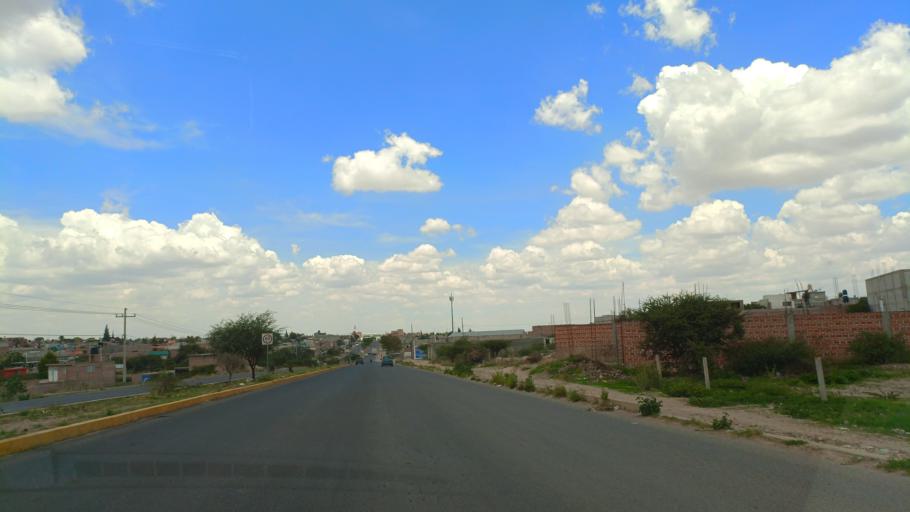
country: MX
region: Guerrero
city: San Luis de la Paz
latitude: 21.2896
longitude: -100.5011
